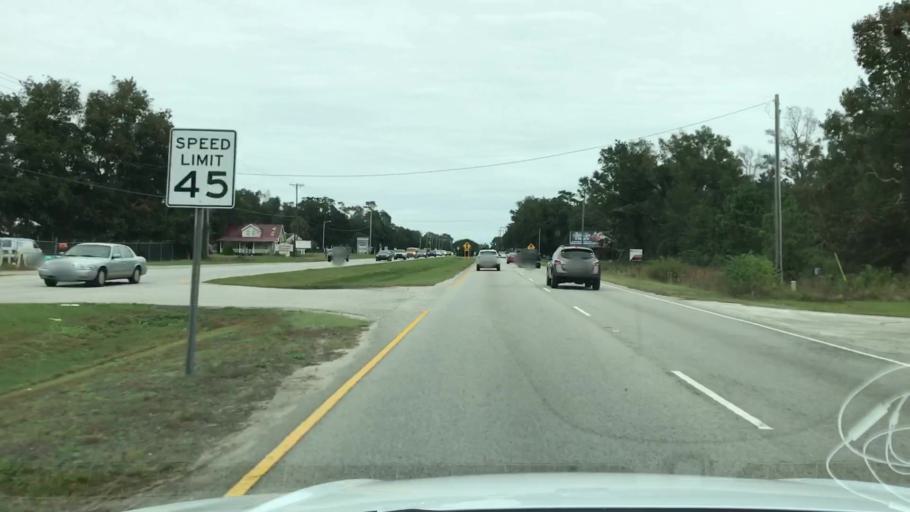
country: US
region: South Carolina
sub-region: Georgetown County
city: Murrells Inlet
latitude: 33.5462
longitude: -79.0506
